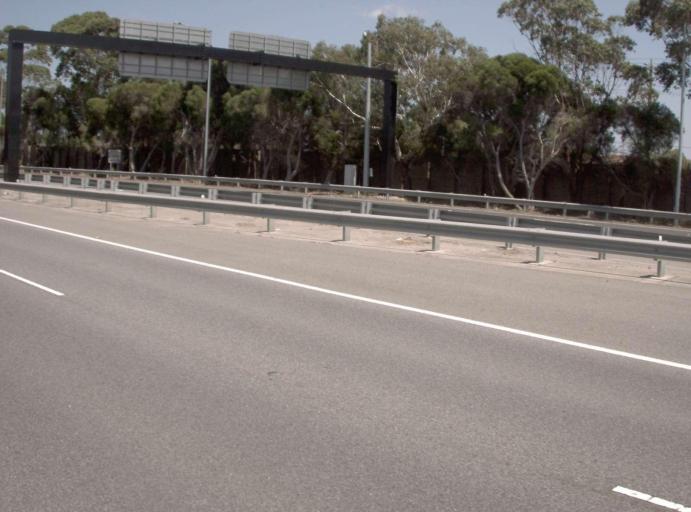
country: AU
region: Victoria
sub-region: Frankston
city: Seaford
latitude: -38.1002
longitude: 145.1428
